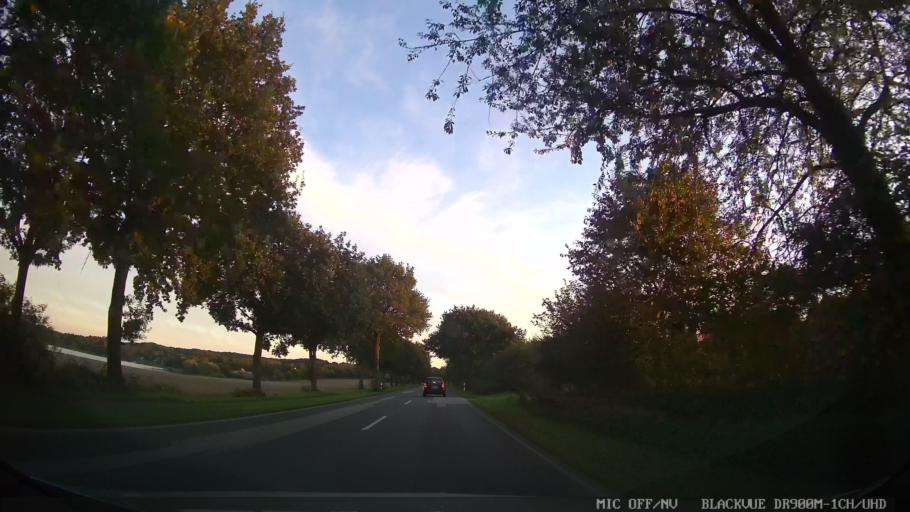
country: DE
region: Schleswig-Holstein
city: Susel
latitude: 54.0322
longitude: 10.6822
